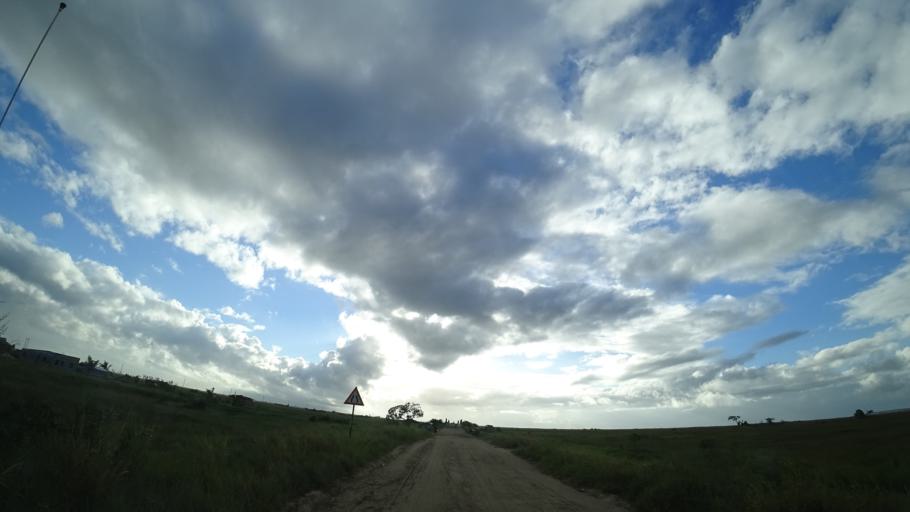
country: MZ
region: Sofala
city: Beira
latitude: -19.7605
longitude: 34.9128
